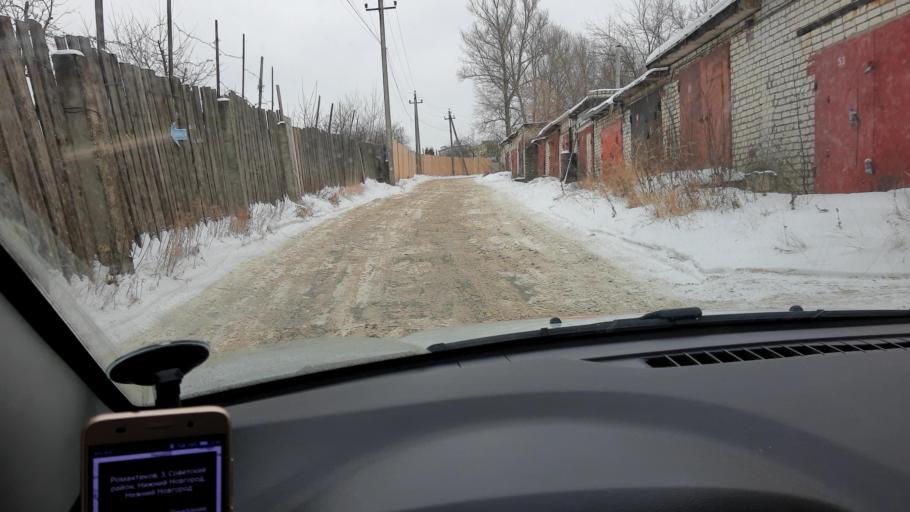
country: RU
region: Nizjnij Novgorod
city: Nizhniy Novgorod
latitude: 56.2490
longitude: 43.9592
